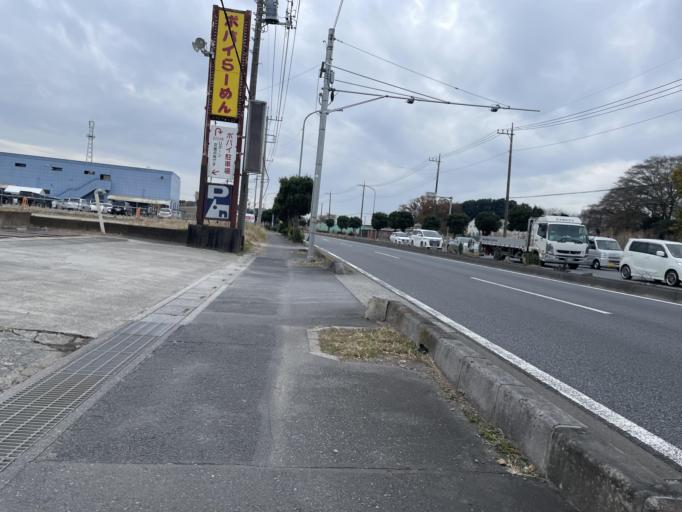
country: JP
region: Saitama
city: Shiraoka
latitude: 36.0008
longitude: 139.6484
